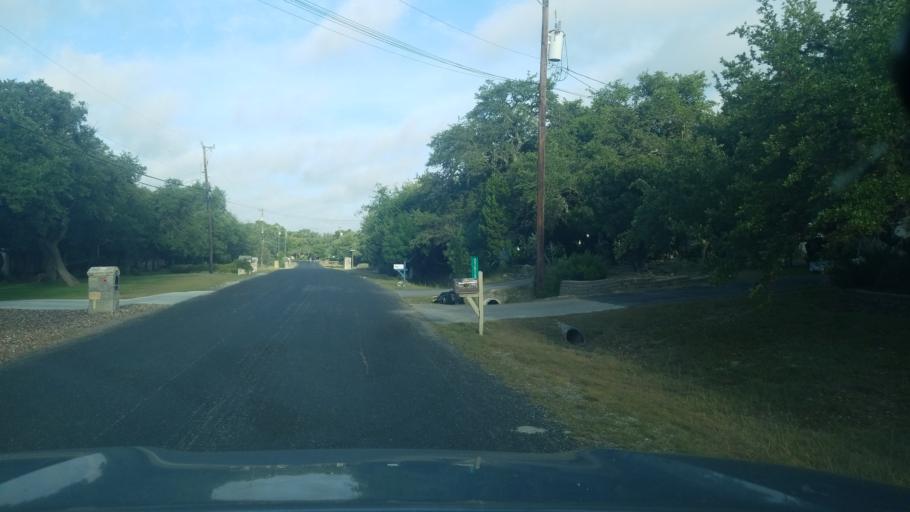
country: US
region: Texas
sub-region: Bexar County
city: Timberwood Park
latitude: 29.6992
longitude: -98.5040
